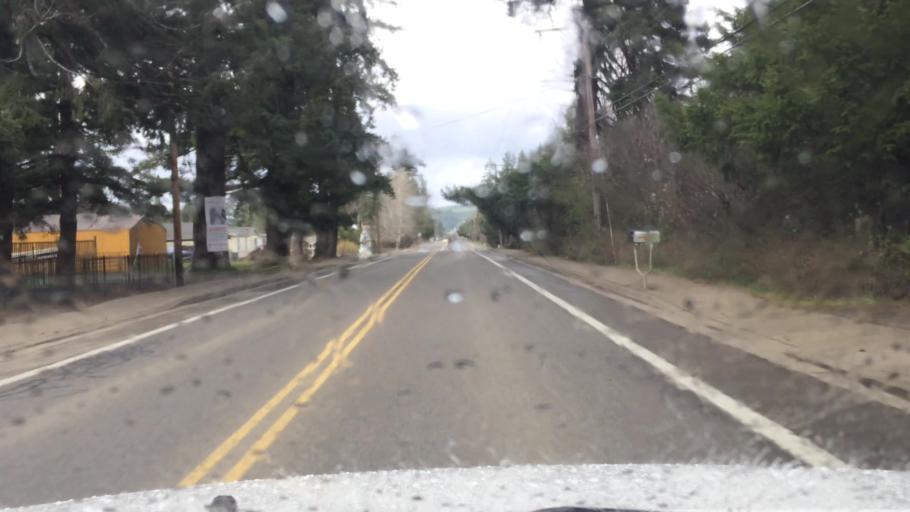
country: US
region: Oregon
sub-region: Polk County
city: Grand Ronde
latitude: 45.0692
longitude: -123.6119
